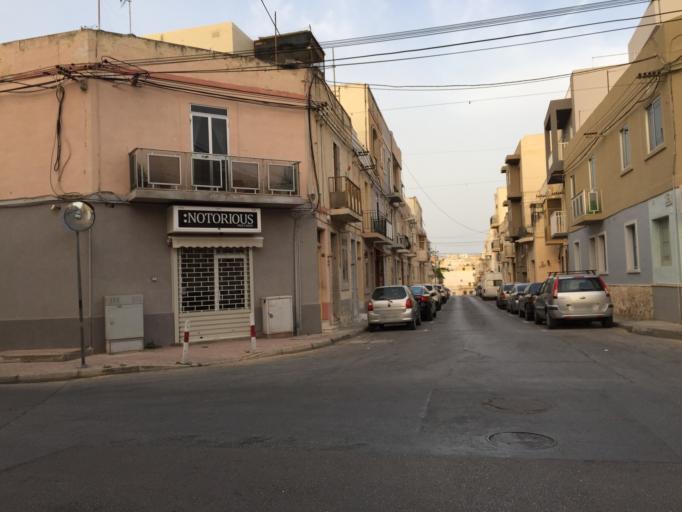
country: MT
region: Il-Fgura
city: Fgura
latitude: 35.8744
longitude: 14.5194
